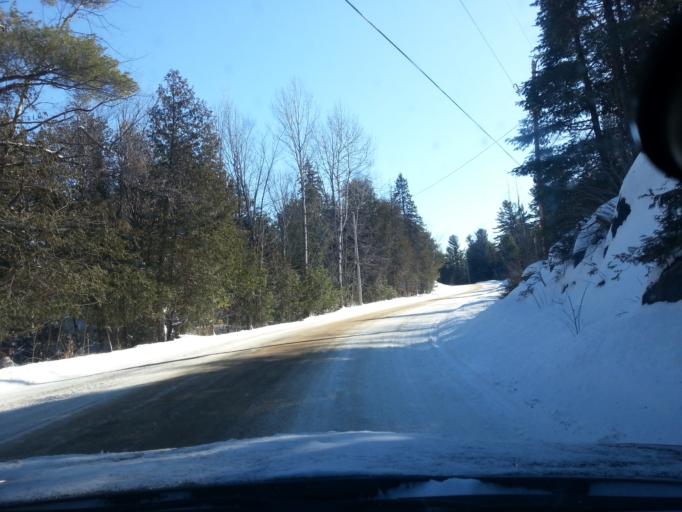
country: CA
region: Ontario
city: Arnprior
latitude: 45.2585
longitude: -76.3214
